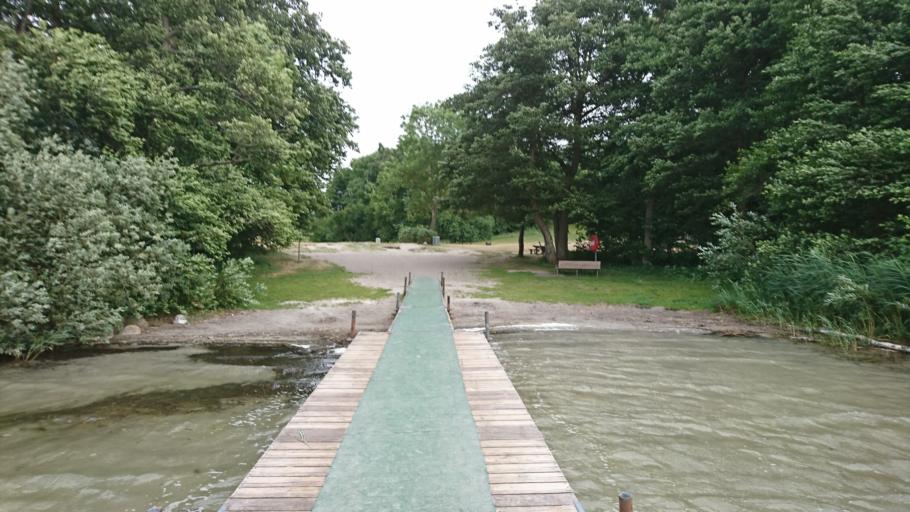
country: DK
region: Capital Region
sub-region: Egedal Kommune
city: Ganlose
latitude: 55.8194
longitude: 12.2323
